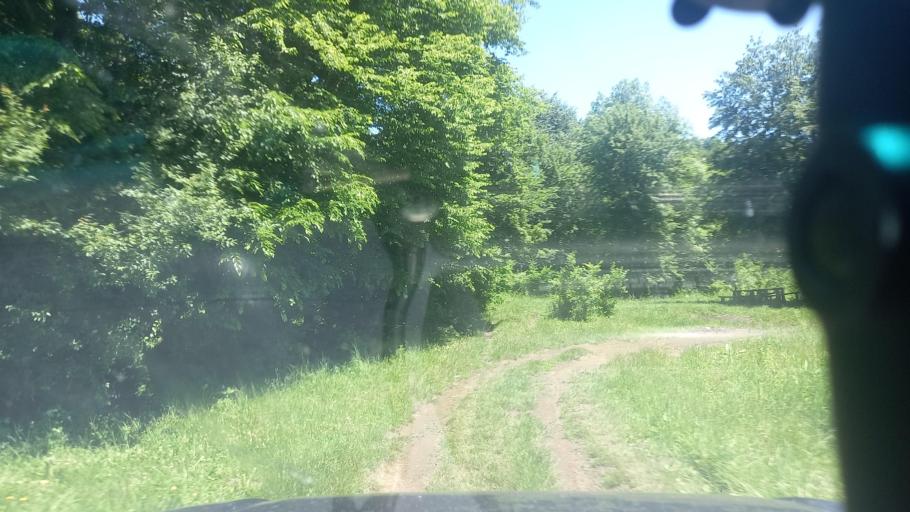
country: RU
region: Karachayevo-Cherkesiya
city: Pregradnaya
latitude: 44.1043
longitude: 41.1369
